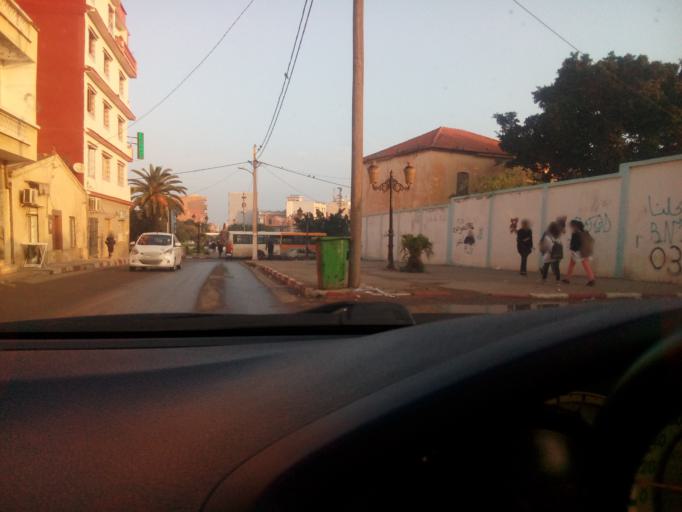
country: DZ
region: Oran
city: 'Ain el Turk
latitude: 35.7418
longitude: -0.7729
